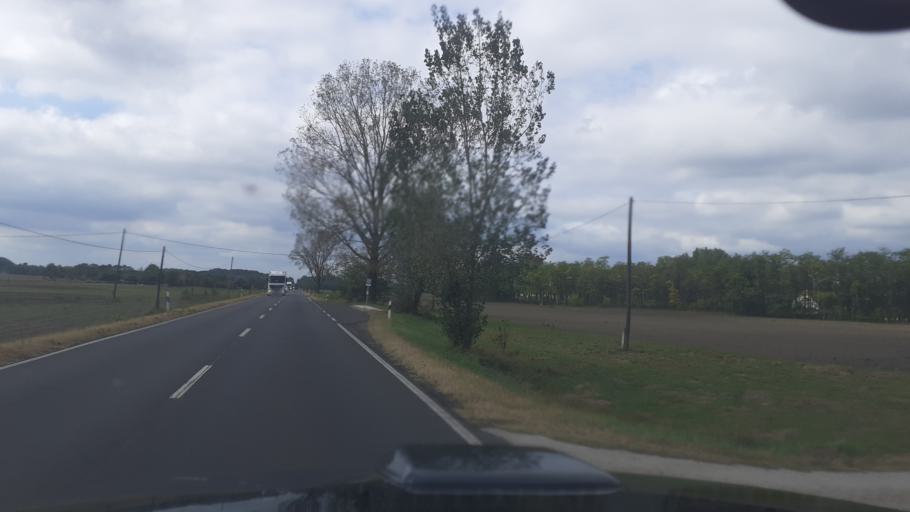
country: HU
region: Bacs-Kiskun
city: Agasegyhaza
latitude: 46.8716
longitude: 19.4426
